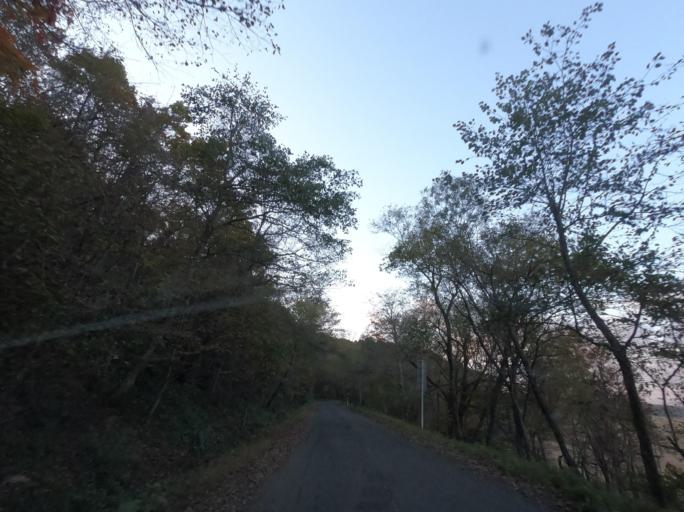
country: JP
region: Hokkaido
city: Kushiro
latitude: 43.1948
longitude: 144.4629
